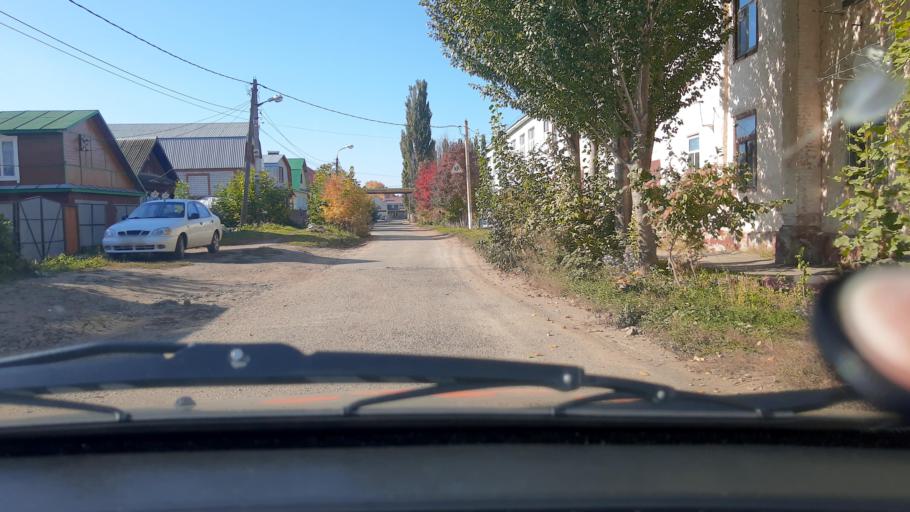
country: RU
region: Bashkortostan
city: Mikhaylovka
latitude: 54.7429
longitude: 55.9026
